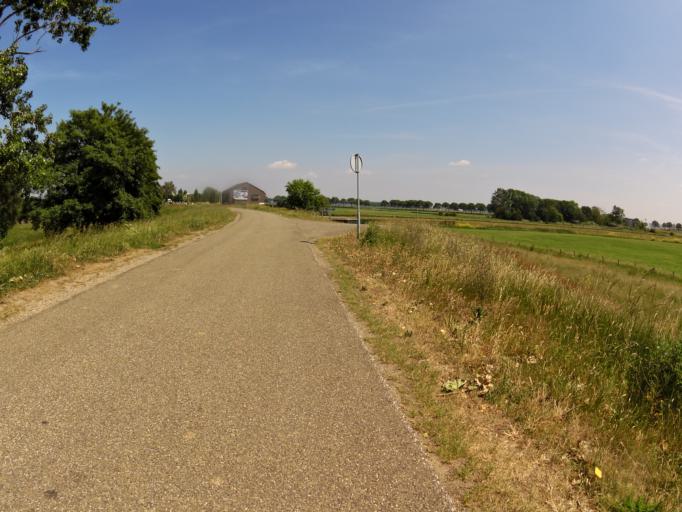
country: NL
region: North Brabant
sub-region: Gemeente 's-Hertogenbosch
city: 's-Hertogenbosch
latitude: 51.7535
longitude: 5.3535
